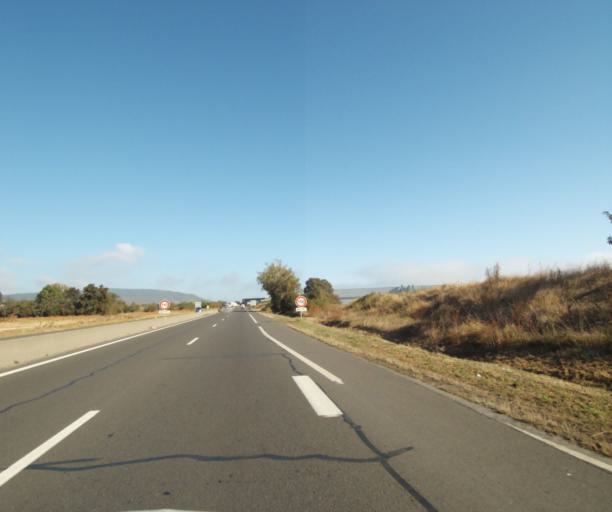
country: FR
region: Auvergne
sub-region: Departement du Puy-de-Dome
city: Cebazat
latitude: 45.8335
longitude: 3.1143
